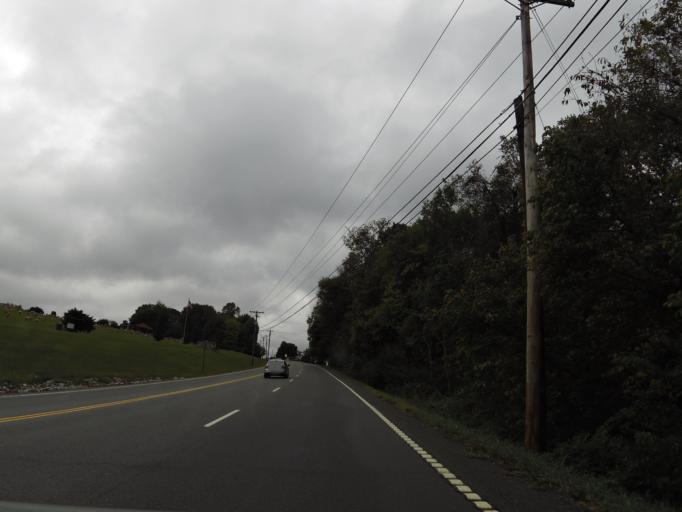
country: US
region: Tennessee
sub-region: Loudon County
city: Lenoir City
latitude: 35.7756
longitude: -84.3011
